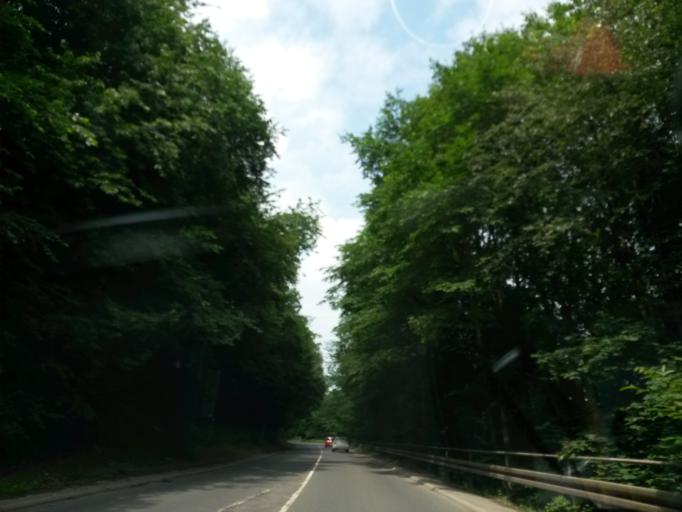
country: DE
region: North Rhine-Westphalia
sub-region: Regierungsbezirk Arnsberg
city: Hagen
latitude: 51.3897
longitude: 7.5237
